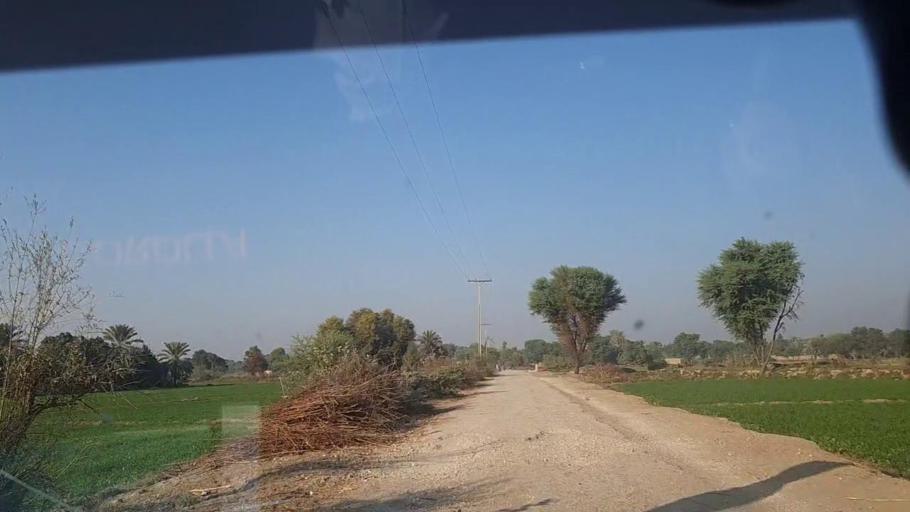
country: PK
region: Sindh
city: Sobhadero
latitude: 27.2517
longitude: 68.3503
